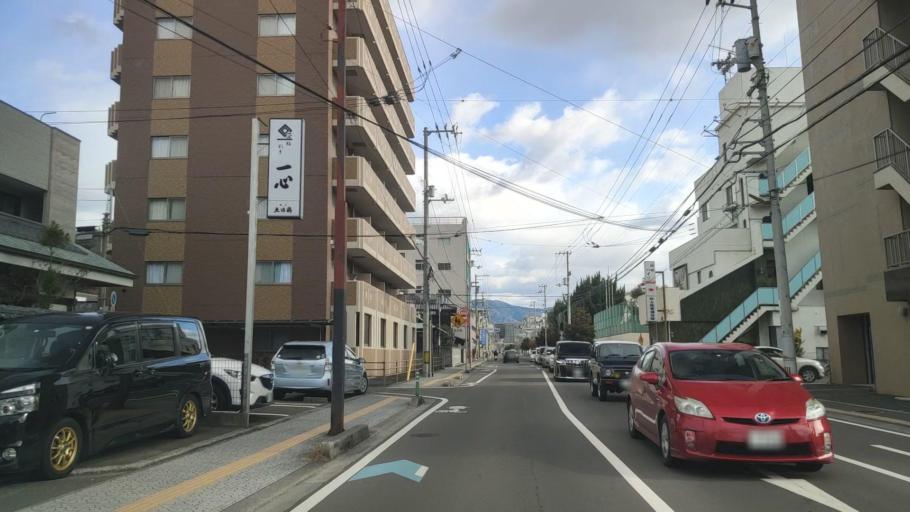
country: JP
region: Ehime
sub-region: Shikoku-chuo Shi
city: Matsuyama
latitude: 33.8526
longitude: 132.7624
